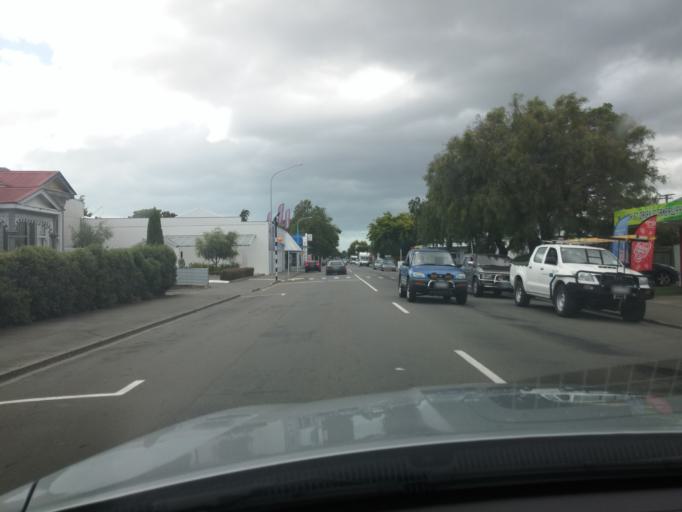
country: NZ
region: Marlborough
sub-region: Marlborough District
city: Blenheim
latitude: -41.5118
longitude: 173.9505
